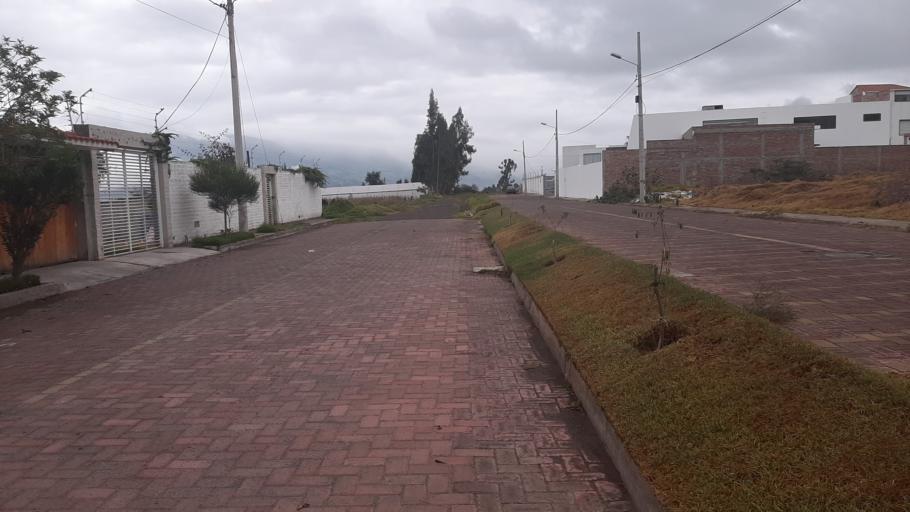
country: EC
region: Chimborazo
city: Riobamba
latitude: -1.6696
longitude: -78.6762
